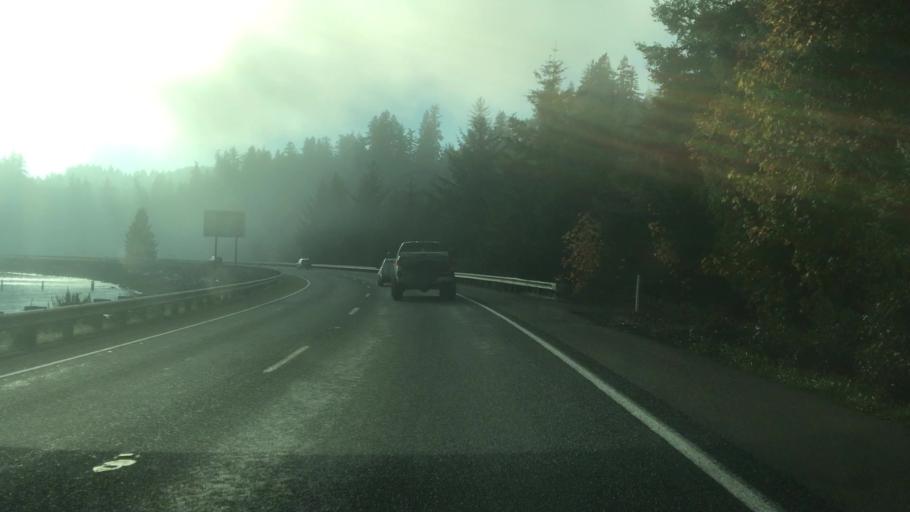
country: US
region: Oregon
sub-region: Clatsop County
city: Astoria
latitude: 46.2699
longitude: -123.8313
